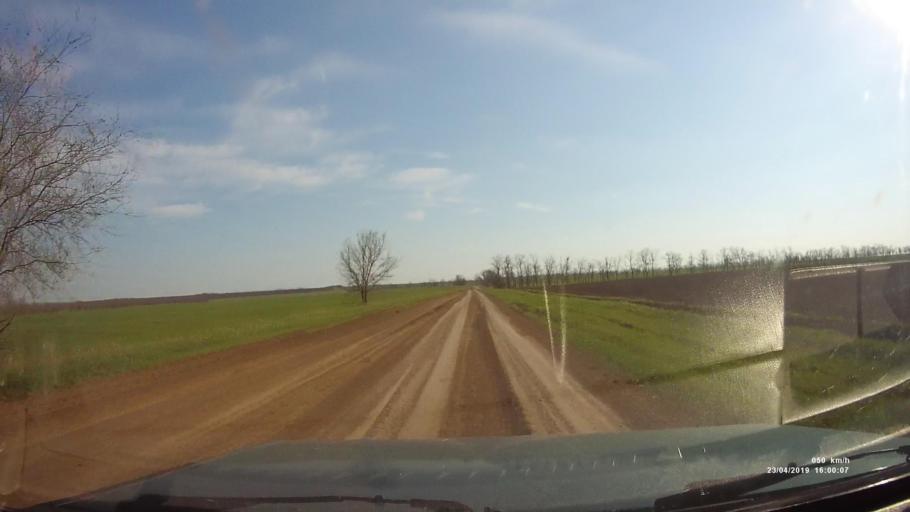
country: RU
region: Rostov
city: Remontnoye
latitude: 46.5116
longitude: 43.1085
